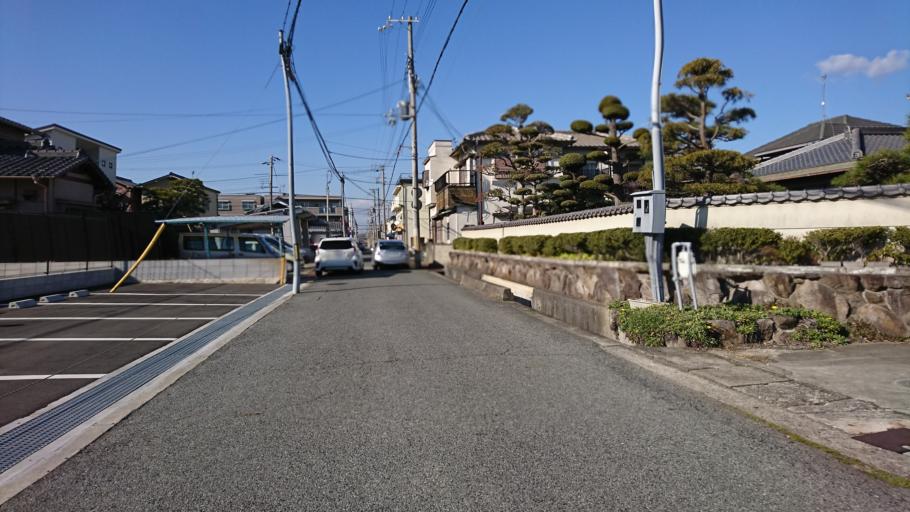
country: JP
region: Hyogo
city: Kakogawacho-honmachi
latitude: 34.7442
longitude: 134.8643
